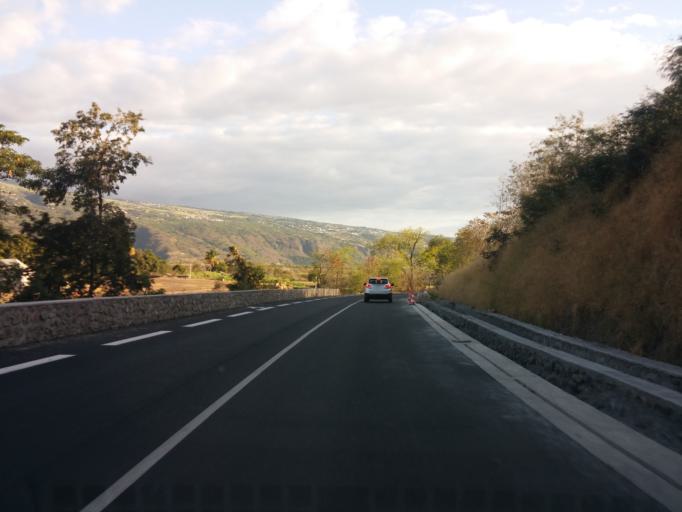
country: RE
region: Reunion
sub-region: Reunion
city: Le Port
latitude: -20.9708
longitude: 55.3090
